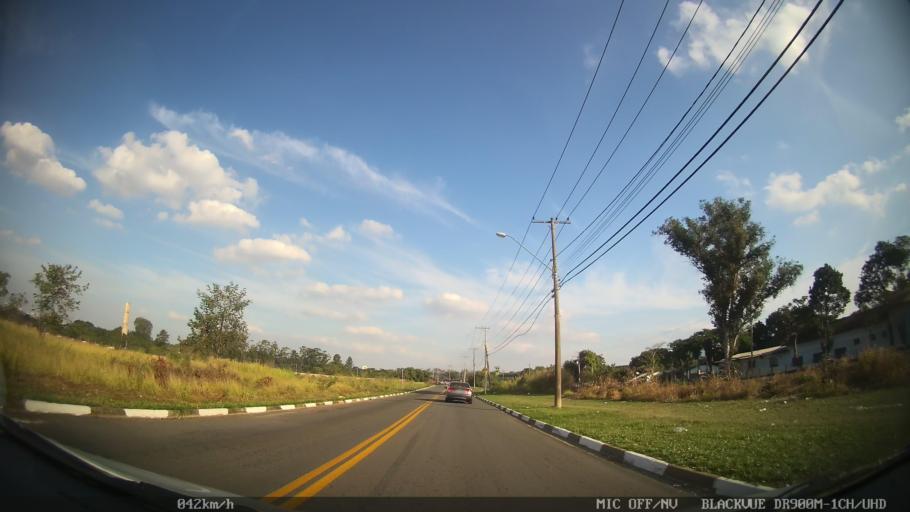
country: BR
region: Sao Paulo
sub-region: Hortolandia
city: Hortolandia
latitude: -22.8709
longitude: -47.1560
